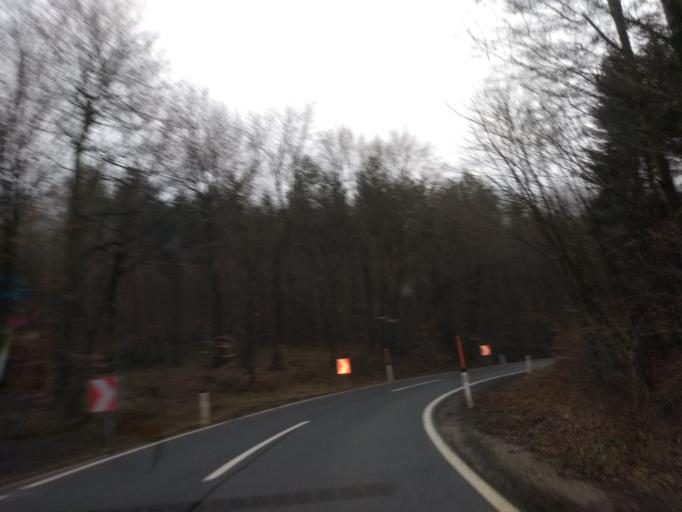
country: AT
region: Lower Austria
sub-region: Politischer Bezirk Tulln
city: Sieghartskirchen
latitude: 48.2282
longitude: 16.0347
